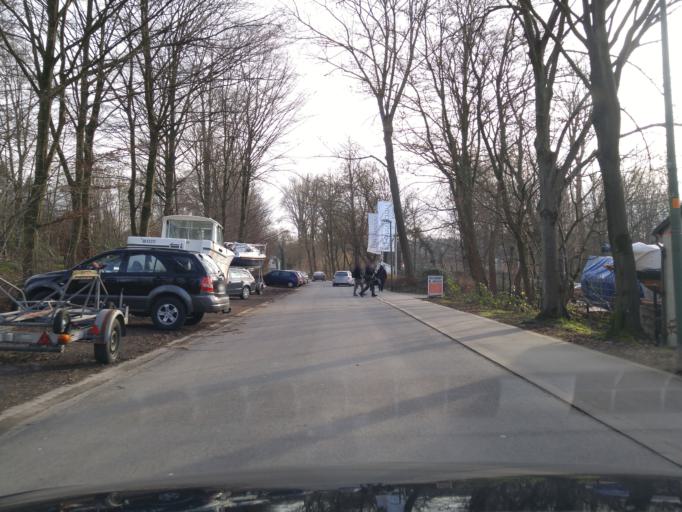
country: DE
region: North Rhine-Westphalia
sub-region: Regierungsbezirk Dusseldorf
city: Velbert
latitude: 51.3950
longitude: 7.0606
